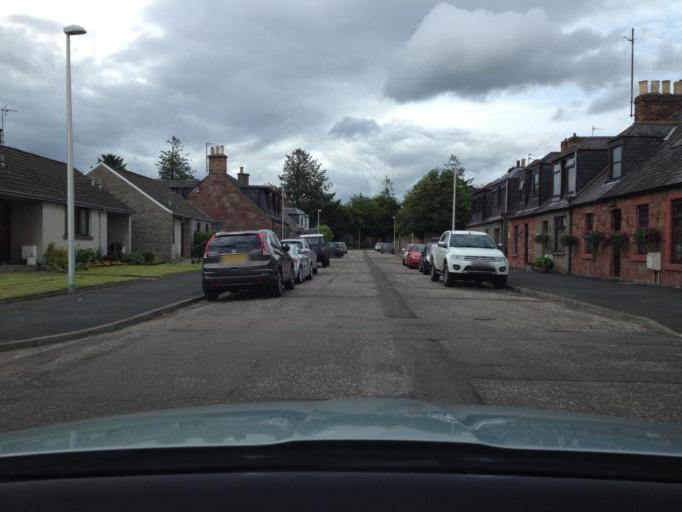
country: GB
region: Scotland
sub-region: Angus
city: Brechin
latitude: 56.8105
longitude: -2.6582
